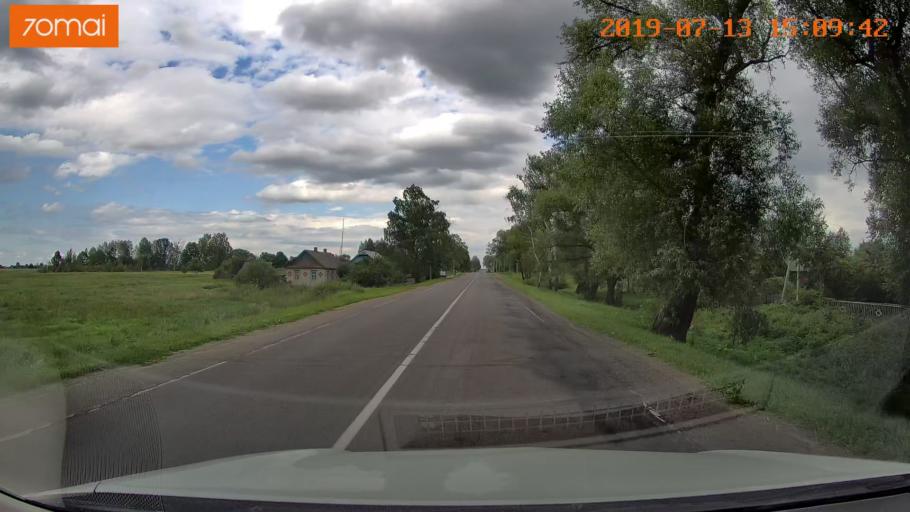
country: BY
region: Mogilev
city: Hlusha
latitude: 53.1720
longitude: 28.7666
